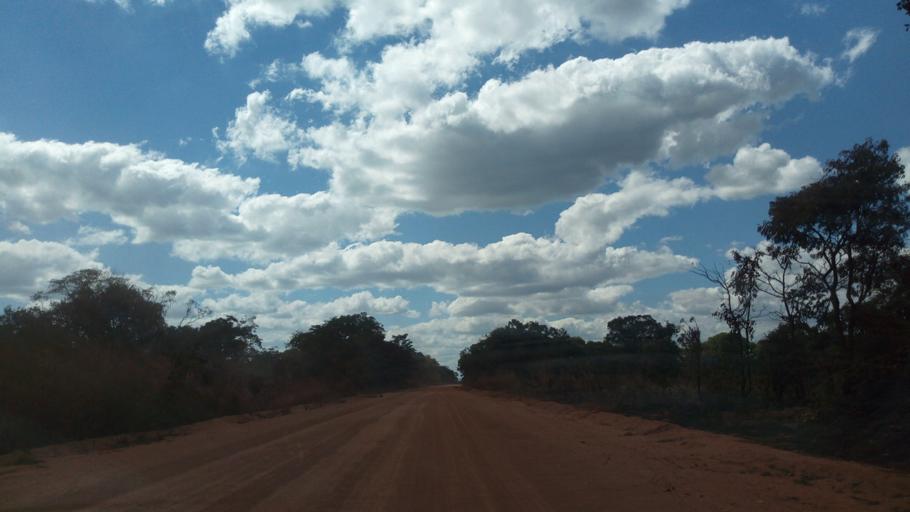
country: ZM
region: Copperbelt
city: Mufulira
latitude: -12.0401
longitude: 28.6683
